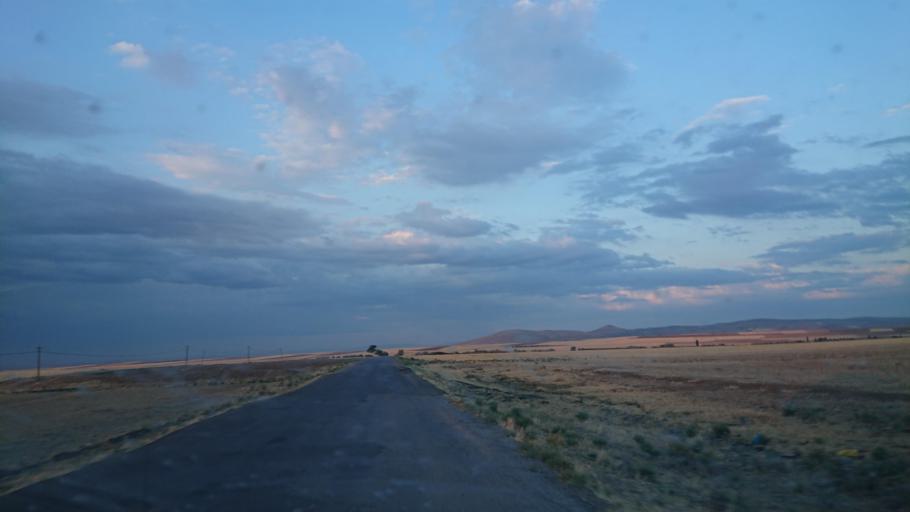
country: TR
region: Aksaray
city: Balci
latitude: 38.8243
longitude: 34.1067
